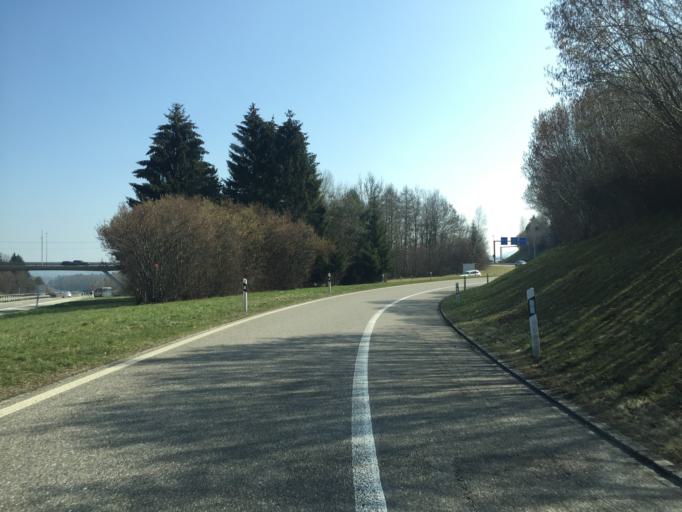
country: CH
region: Saint Gallen
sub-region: Wahlkreis Wil
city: Wil
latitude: 47.4537
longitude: 9.0511
